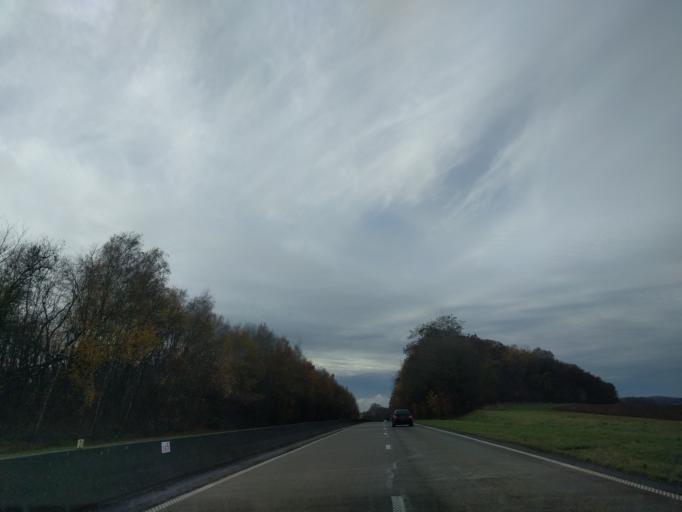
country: BE
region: Wallonia
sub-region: Province de Namur
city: Houyet
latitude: 50.2521
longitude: 5.0159
